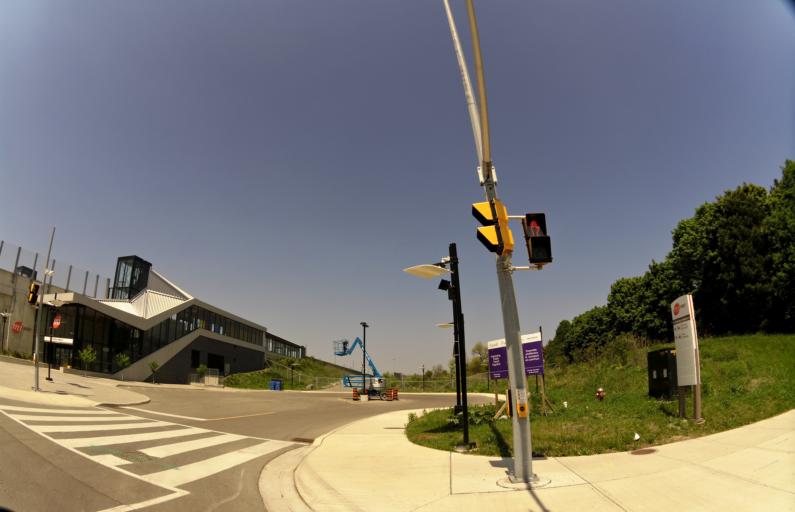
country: CA
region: Ontario
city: Mississauga
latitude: 43.6075
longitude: -79.6360
